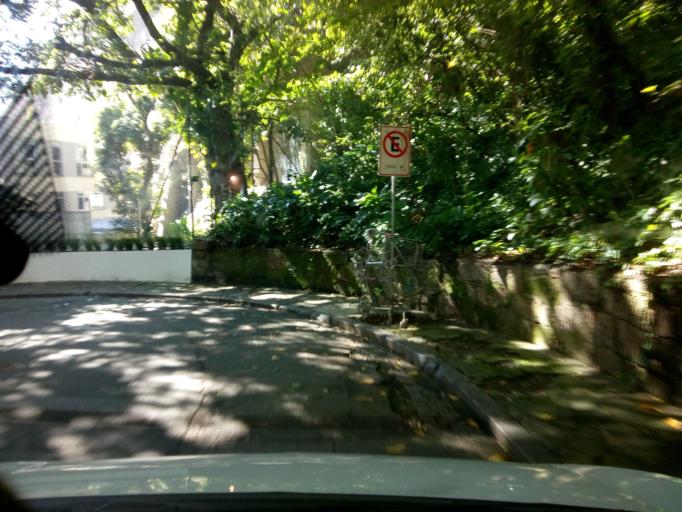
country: BR
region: Rio de Janeiro
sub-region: Rio De Janeiro
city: Rio de Janeiro
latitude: -22.9887
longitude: -43.2291
